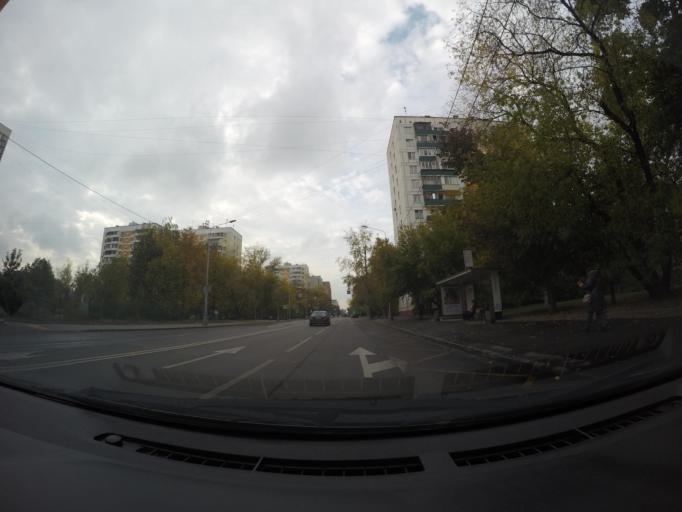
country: RU
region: Moskovskaya
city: Novogireyevo
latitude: 55.7546
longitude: 37.8172
